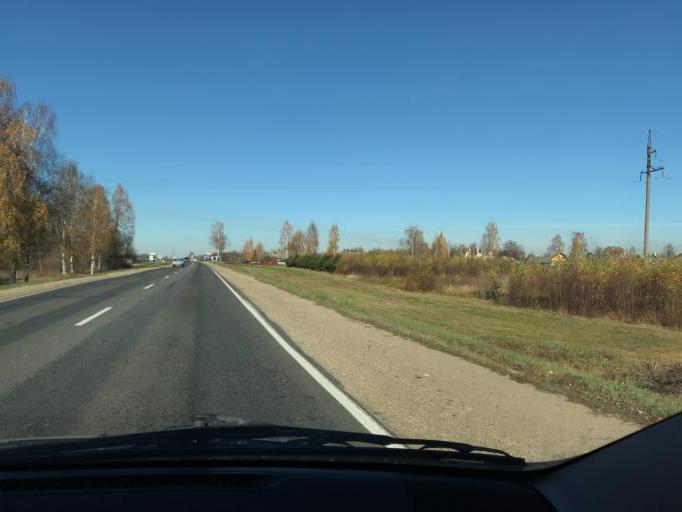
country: BY
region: Vitebsk
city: Polatsk
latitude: 55.4513
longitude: 28.7686
